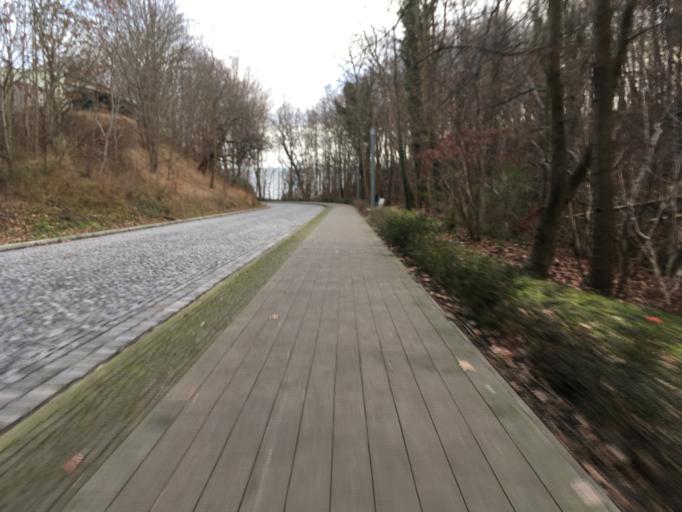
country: DE
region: Mecklenburg-Vorpommern
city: Sassnitz
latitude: 54.5078
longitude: 13.6271
